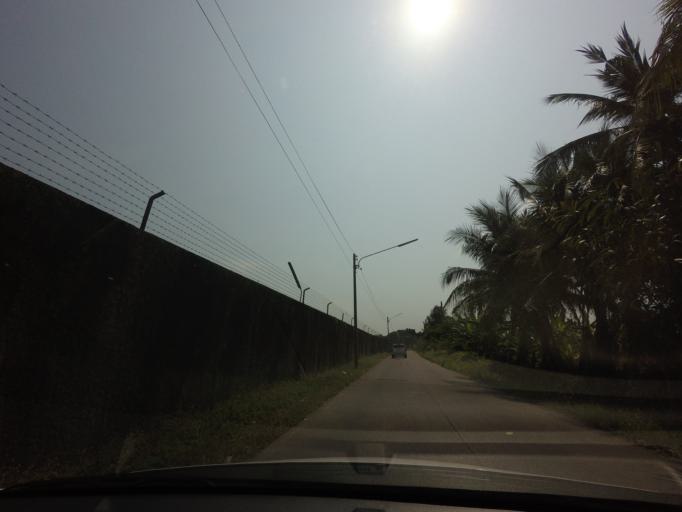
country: TH
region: Nakhon Pathom
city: Sam Phran
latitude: 13.7372
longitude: 100.2647
